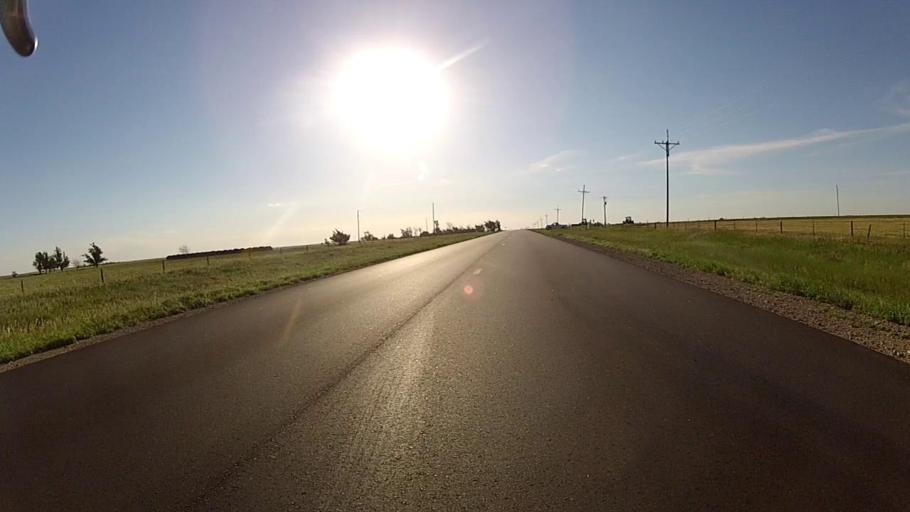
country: US
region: Kansas
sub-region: Comanche County
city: Coldwater
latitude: 37.2820
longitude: -99.1387
